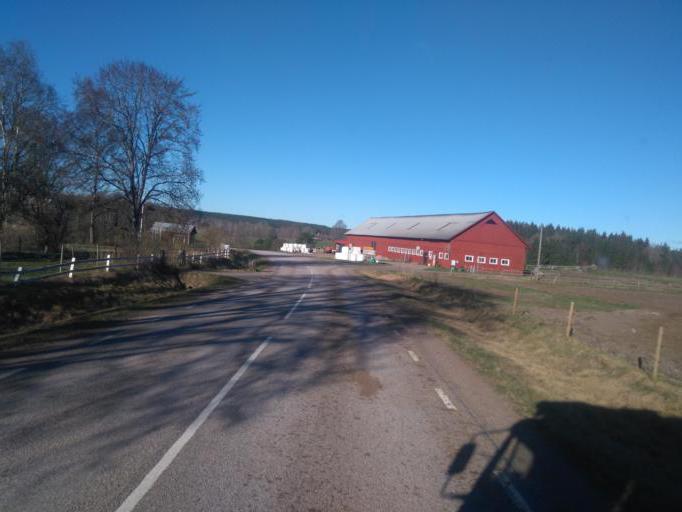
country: SE
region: Joenkoeping
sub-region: Vetlanda Kommun
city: Vetlanda
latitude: 57.4798
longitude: 15.1846
